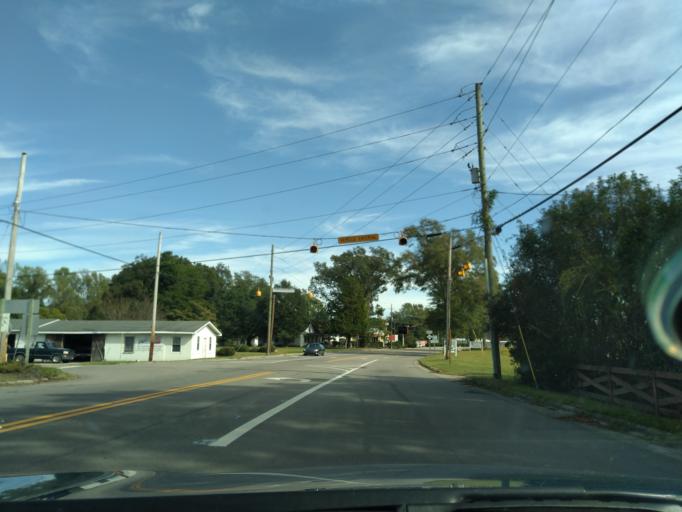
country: US
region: North Carolina
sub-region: Beaufort County
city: Washington
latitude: 35.5343
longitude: -77.0252
